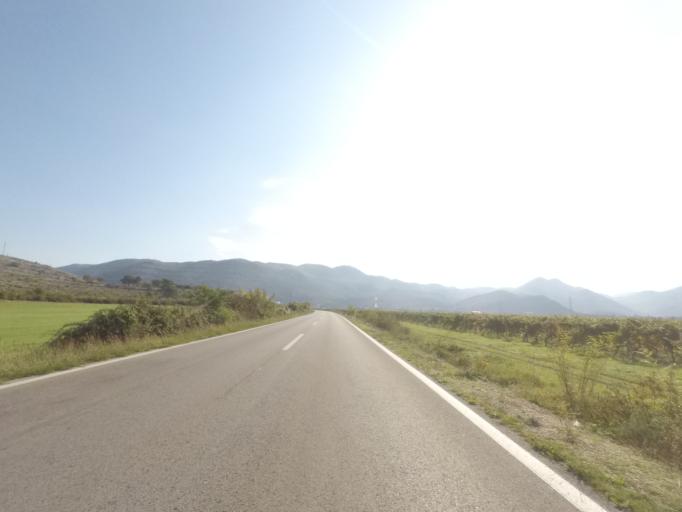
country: BA
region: Republika Srpska
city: Trebinje
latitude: 42.6856
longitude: 18.3179
